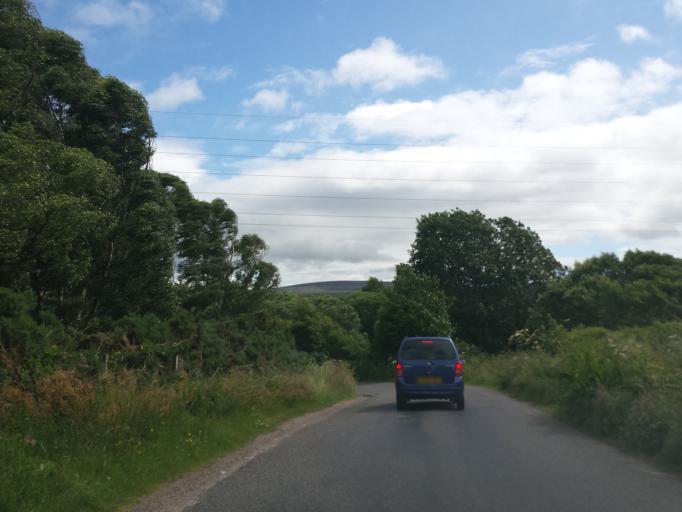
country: GB
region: Scotland
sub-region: Highland
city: Fortrose
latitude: 57.4765
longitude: -4.0765
